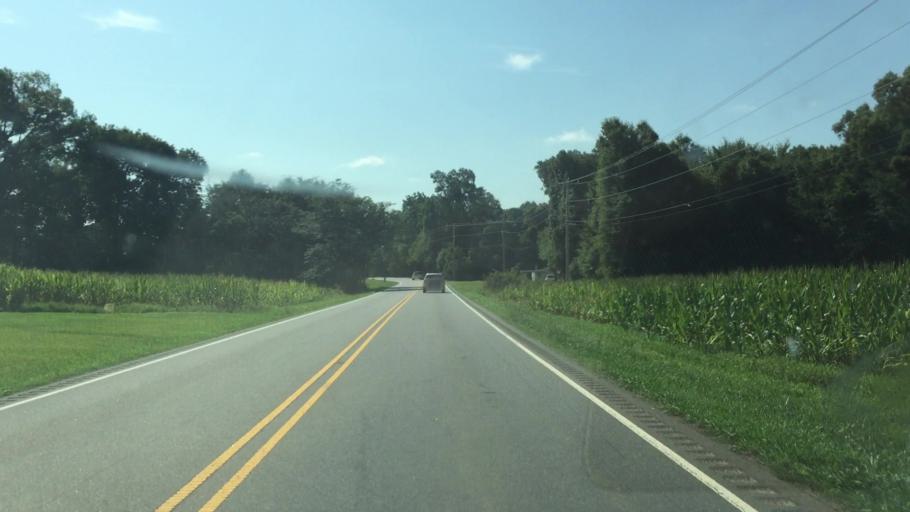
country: US
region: North Carolina
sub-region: Union County
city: Fairview
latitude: 35.1549
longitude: -80.5613
